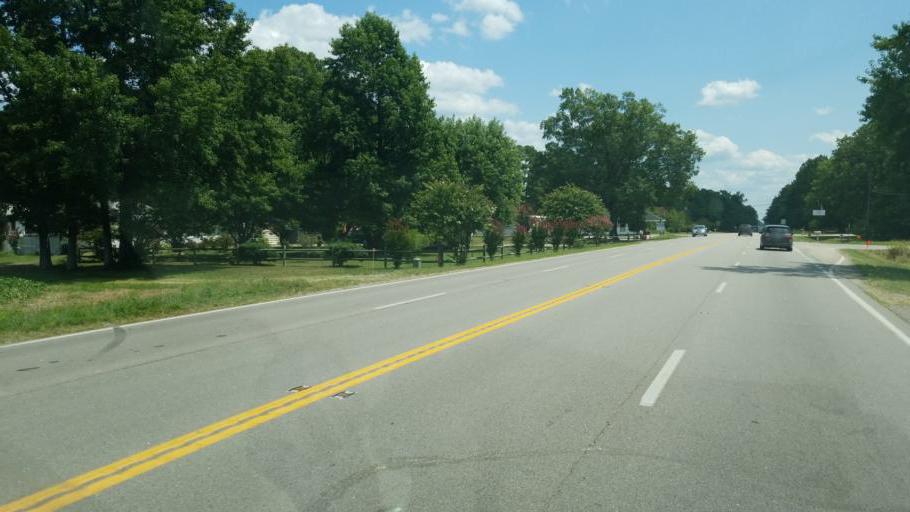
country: US
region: Virginia
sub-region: Prince George County
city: Prince George
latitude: 37.1798
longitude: -77.3124
